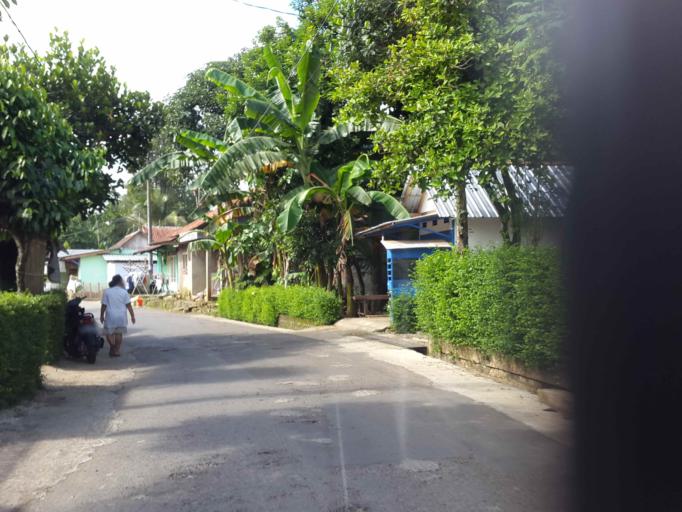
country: ID
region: Central Java
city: Purwokerto
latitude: -7.4189
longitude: 109.1878
